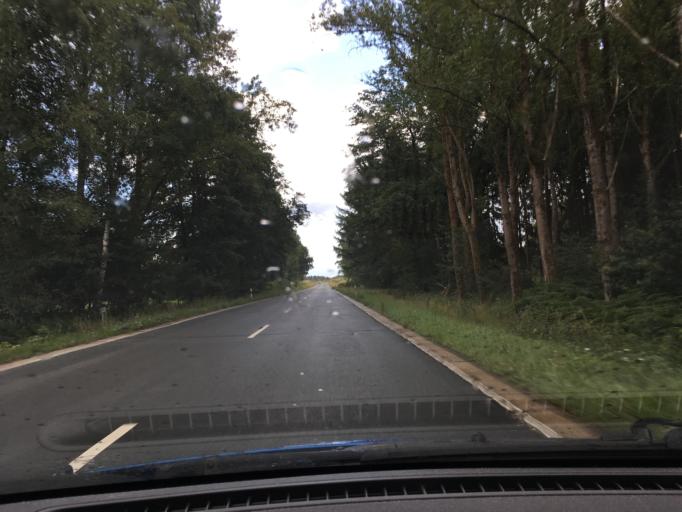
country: DE
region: Lower Saxony
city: Wietzendorf
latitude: 52.9631
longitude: 9.9641
